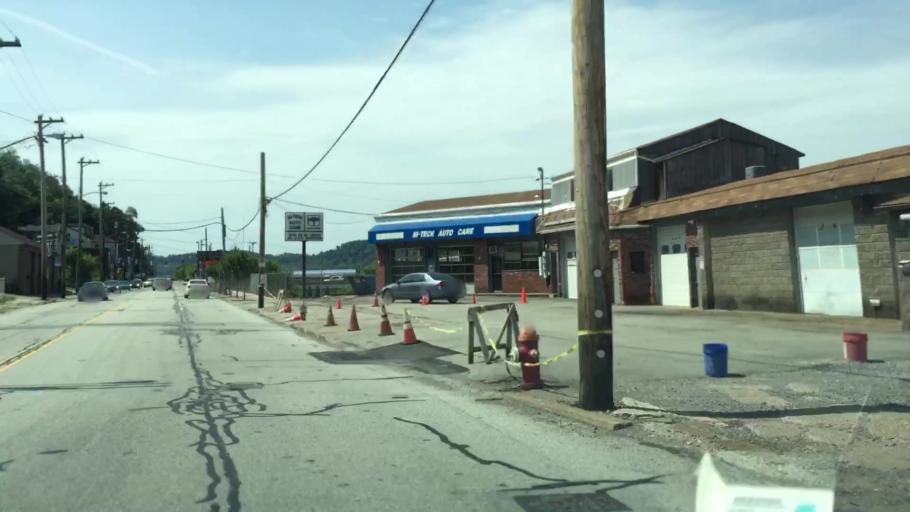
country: US
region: Pennsylvania
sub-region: Allegheny County
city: Sharpsburg
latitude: 40.4892
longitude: -79.9351
